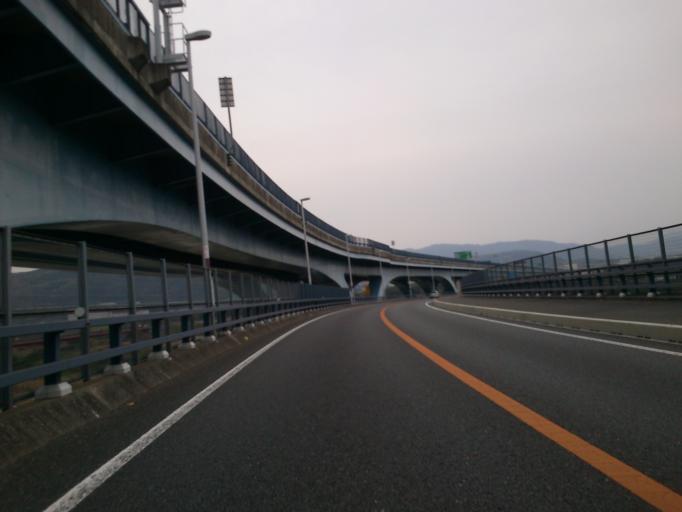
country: JP
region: Kyoto
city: Yawata
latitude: 34.8913
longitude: 135.7053
